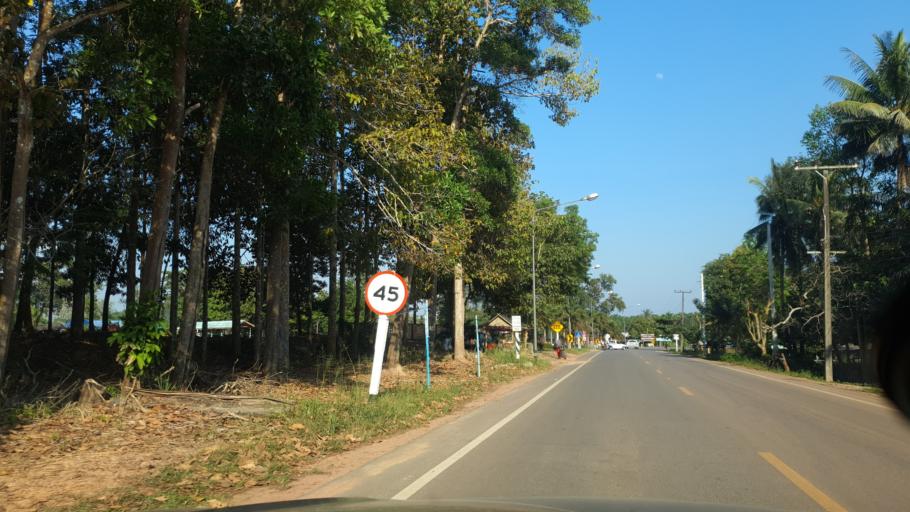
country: TH
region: Chumphon
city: Pathio
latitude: 10.7489
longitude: 99.3320
